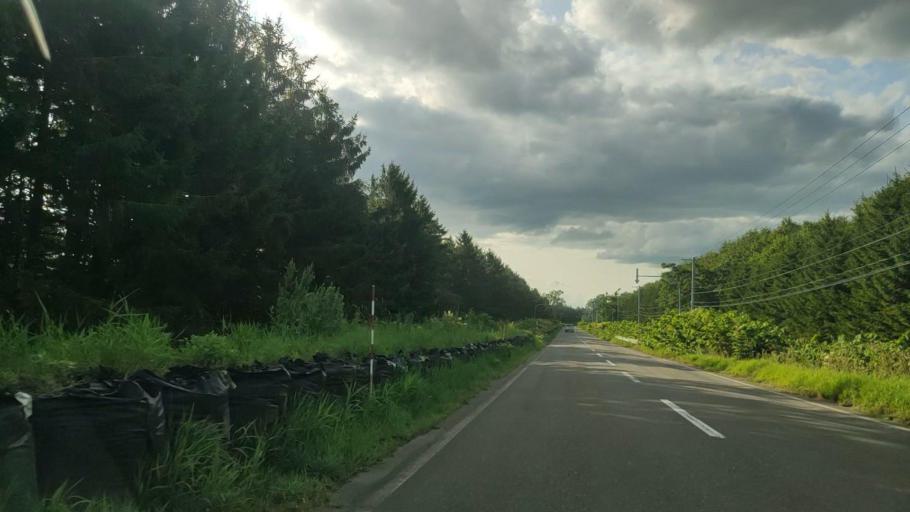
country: JP
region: Hokkaido
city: Makubetsu
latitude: 44.9026
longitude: 141.9083
